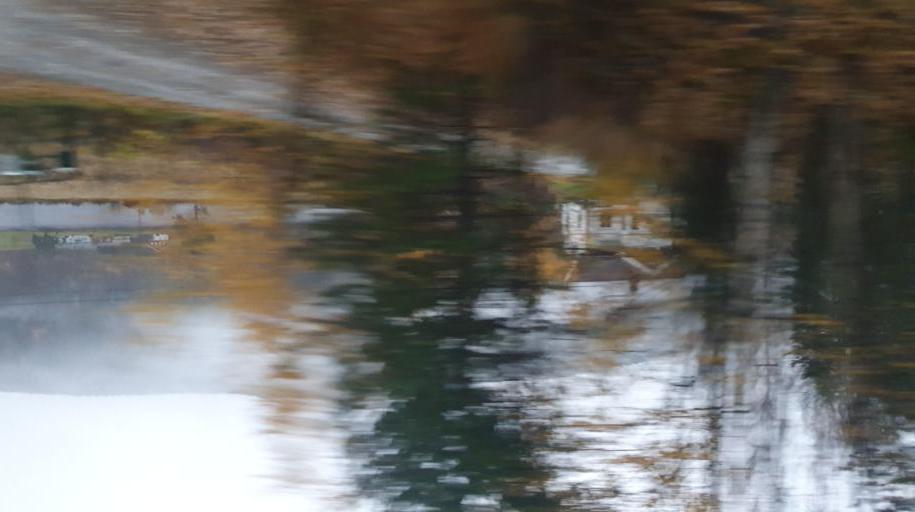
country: NO
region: Buskerud
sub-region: Krodsherad
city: Noresund
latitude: 60.1859
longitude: 9.6136
